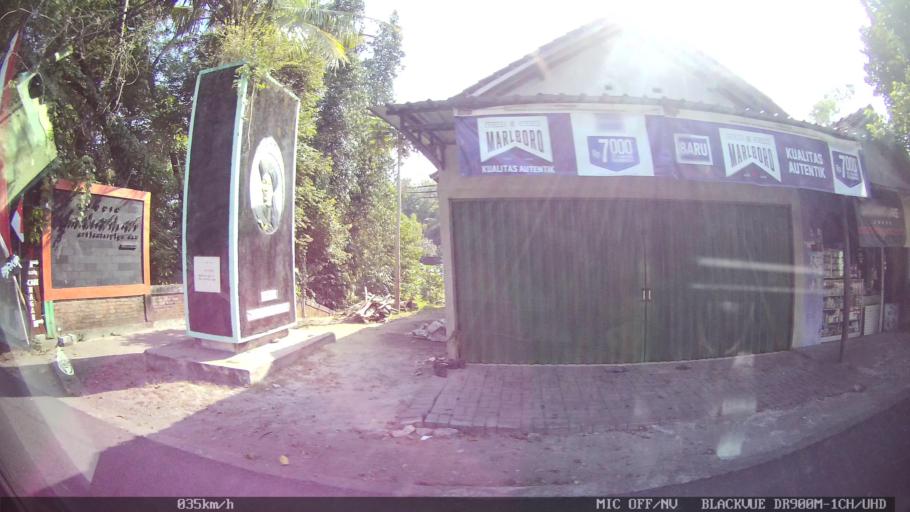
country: ID
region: Daerah Istimewa Yogyakarta
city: Kasihan
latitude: -7.8316
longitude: 110.3386
